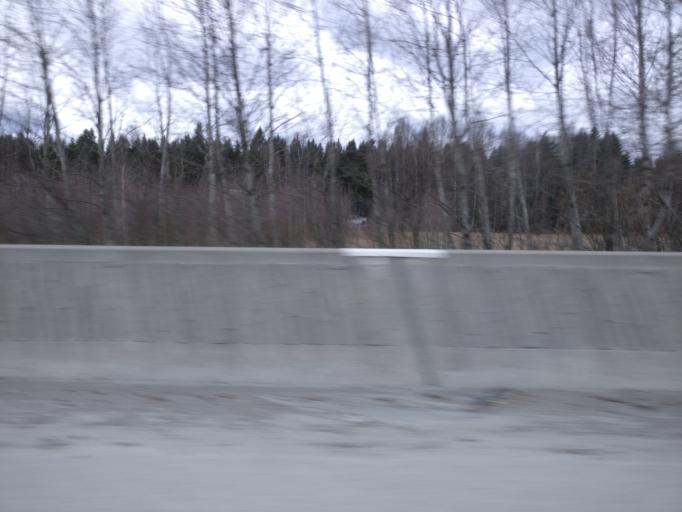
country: FI
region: Haeme
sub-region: Haemeenlinna
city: Parola
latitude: 61.0307
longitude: 24.3930
